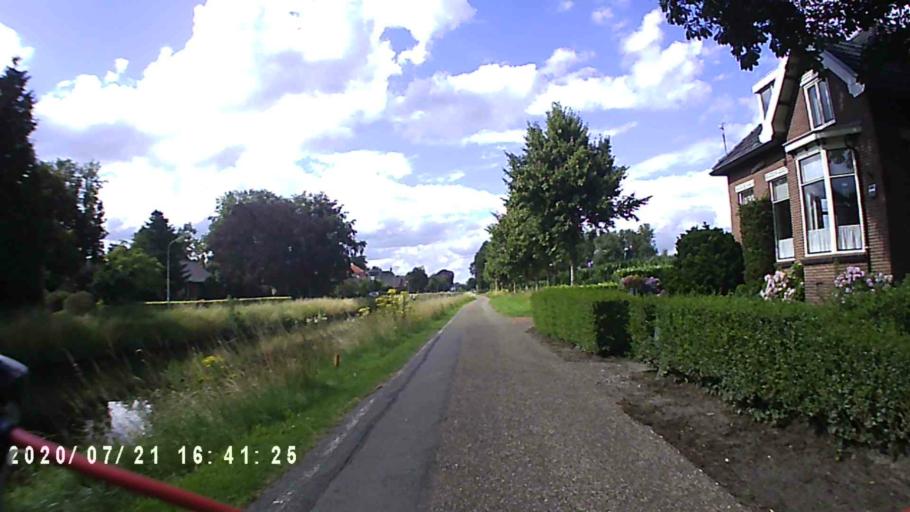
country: NL
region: Groningen
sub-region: Gemeente Hoogezand-Sappemeer
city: Sappemeer
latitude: 53.1008
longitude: 6.7882
